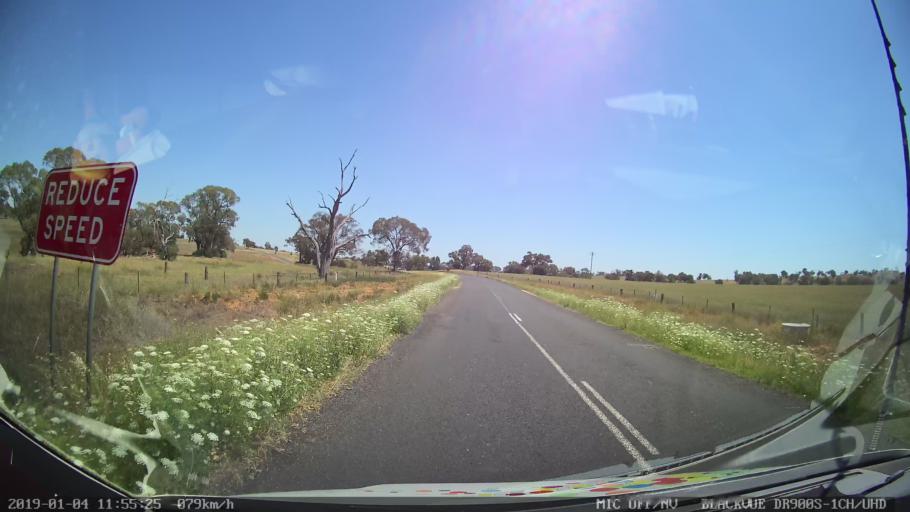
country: AU
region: New South Wales
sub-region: Cabonne
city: Molong
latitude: -32.8545
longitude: 148.7237
